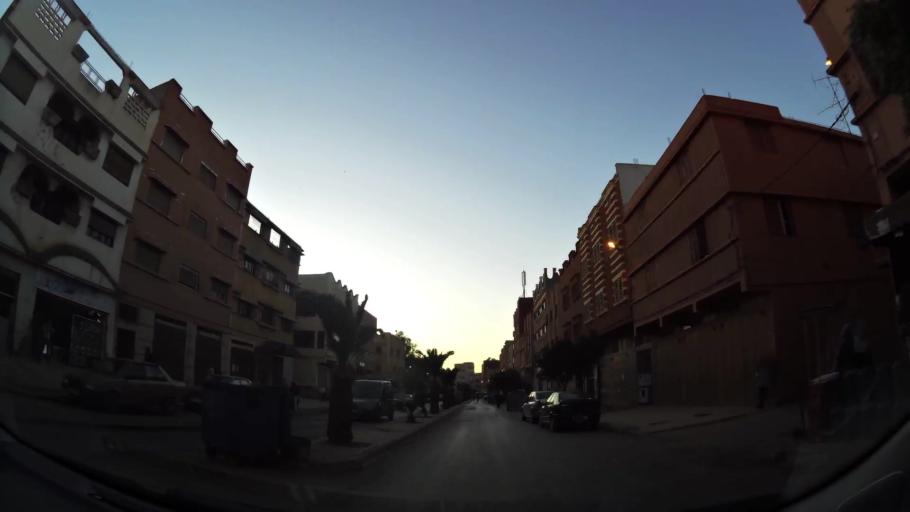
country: MA
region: Oriental
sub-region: Berkane-Taourirt
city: Berkane
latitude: 34.9201
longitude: -2.3212
